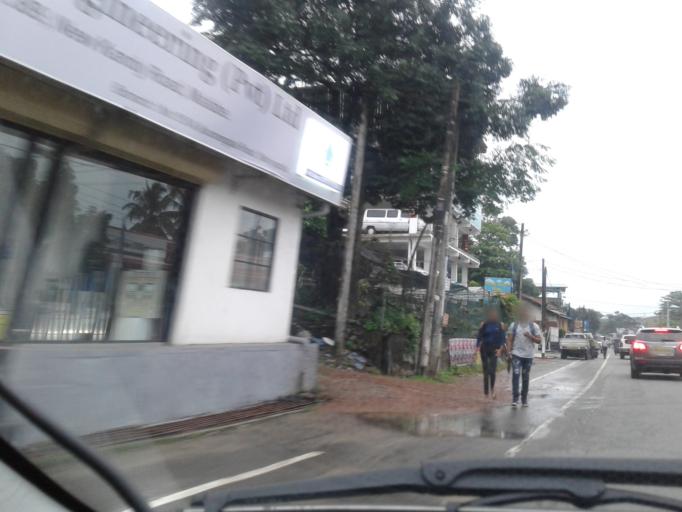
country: LK
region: Western
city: Battaramulla South
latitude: 6.9033
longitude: 79.9583
